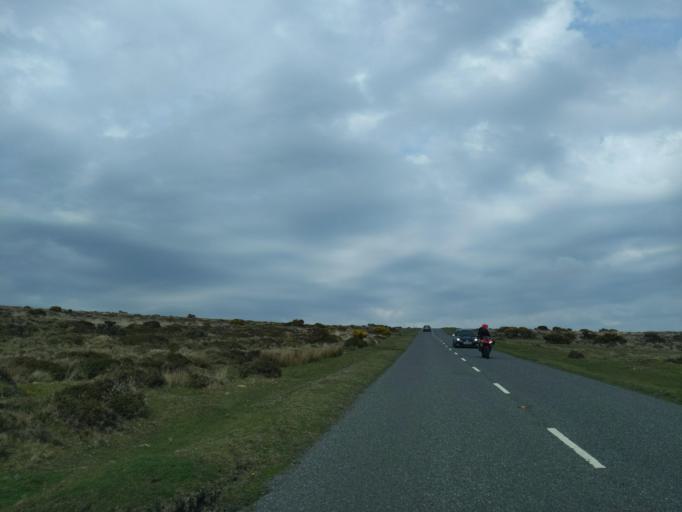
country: GB
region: England
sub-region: Devon
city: Ashburton
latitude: 50.6033
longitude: -3.8960
